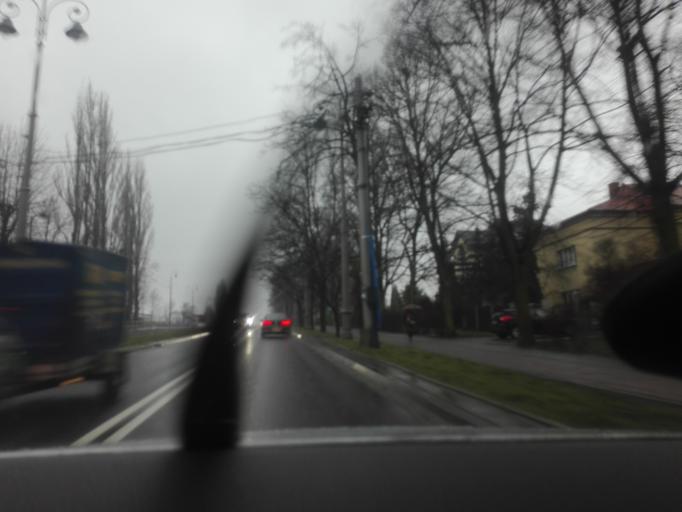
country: PL
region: Silesian Voivodeship
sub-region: Katowice
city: Katowice
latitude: 50.2496
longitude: 19.0132
